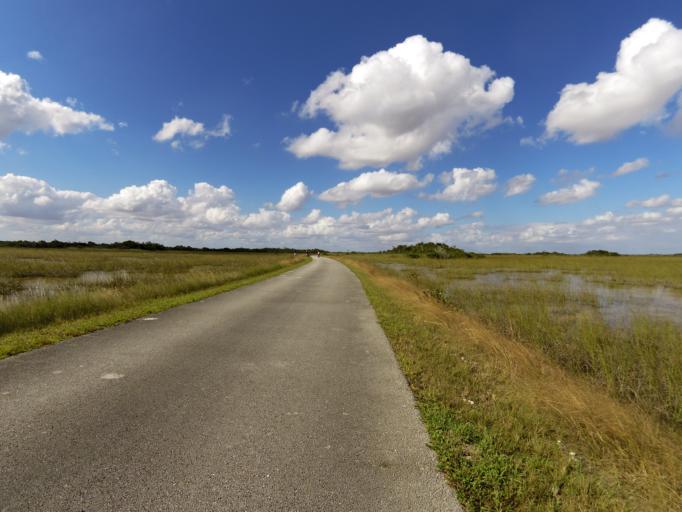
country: US
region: Florida
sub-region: Miami-Dade County
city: The Hammocks
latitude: 25.7054
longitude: -80.7611
